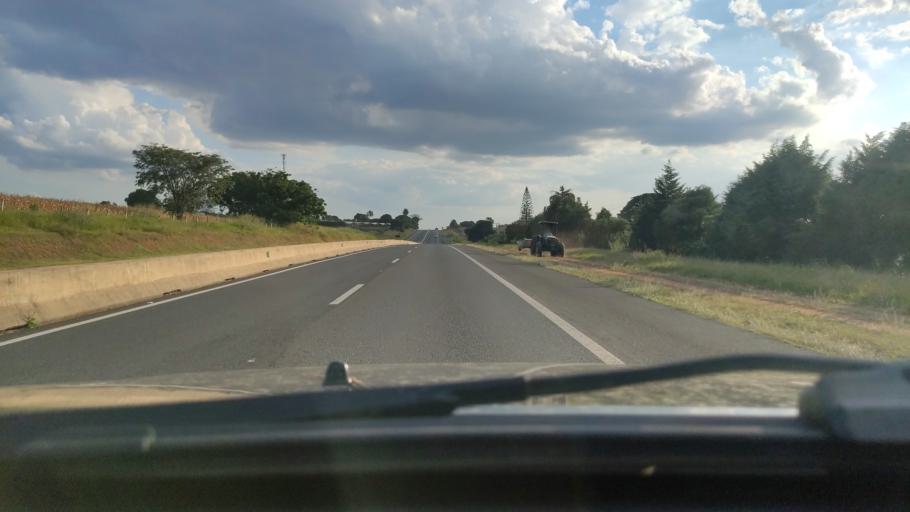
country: BR
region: Sao Paulo
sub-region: Artur Nogueira
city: Artur Nogueira
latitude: -22.4622
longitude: -47.1026
